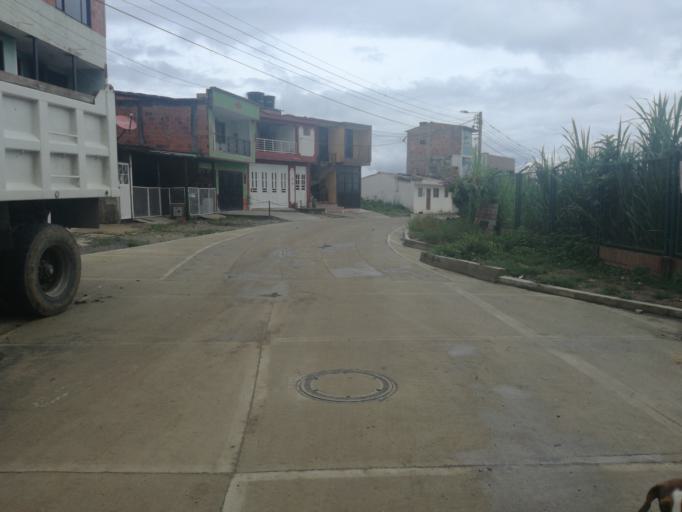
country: CO
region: Boyaca
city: Santana
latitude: 6.0589
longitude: -73.4837
